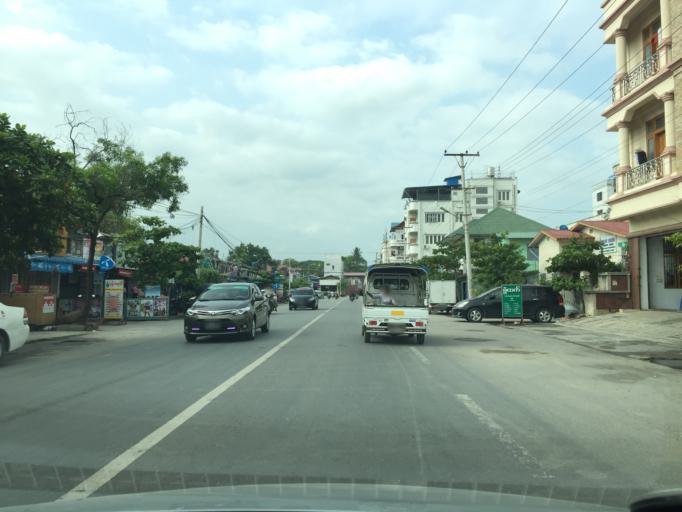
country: MM
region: Mandalay
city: Mandalay
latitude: 21.9694
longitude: 96.1029
